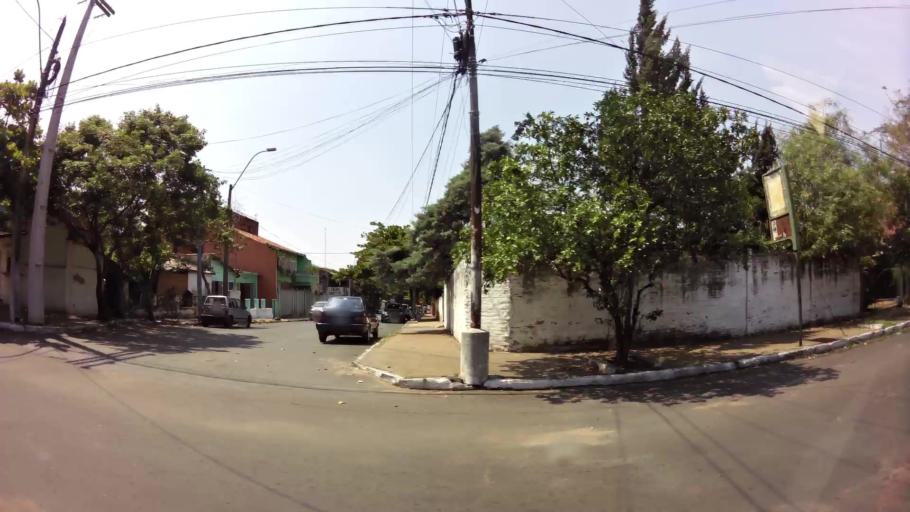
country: PY
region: Asuncion
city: Asuncion
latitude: -25.2966
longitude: -57.6542
